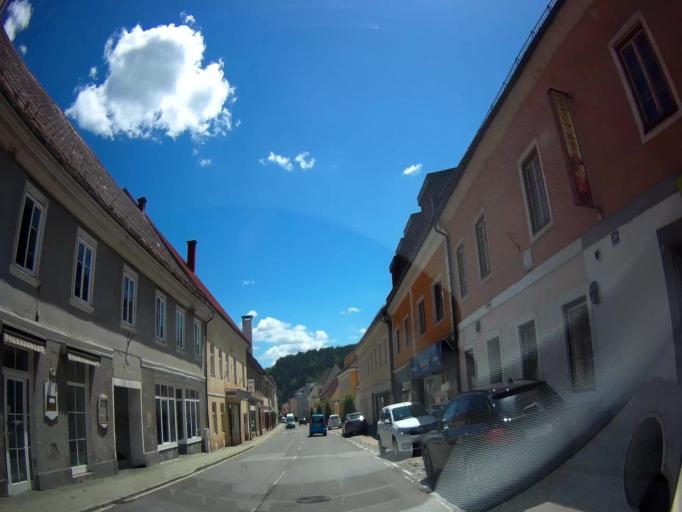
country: AT
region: Carinthia
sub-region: Politischer Bezirk Sankt Veit an der Glan
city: Sankt Veit an der Glan
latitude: 46.7659
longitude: 14.3603
